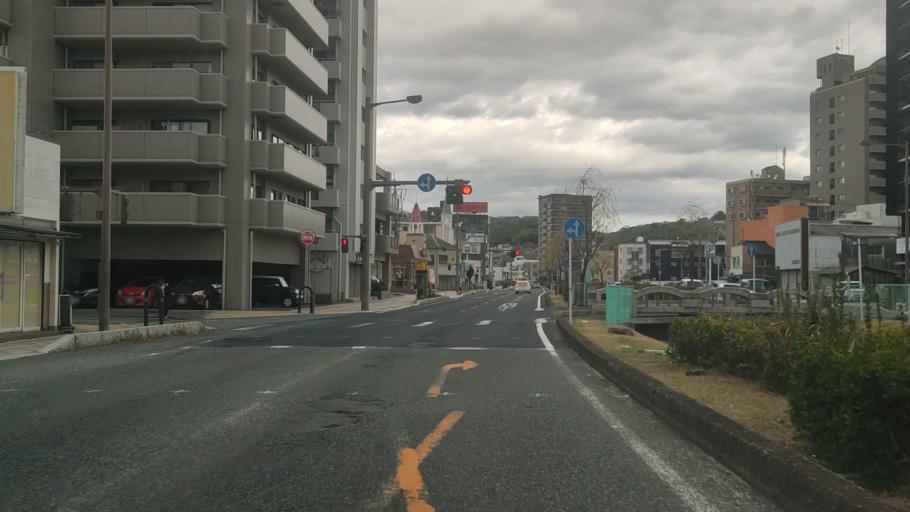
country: JP
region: Yamaguchi
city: Shimonoseki
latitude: 33.9614
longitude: 130.9416
